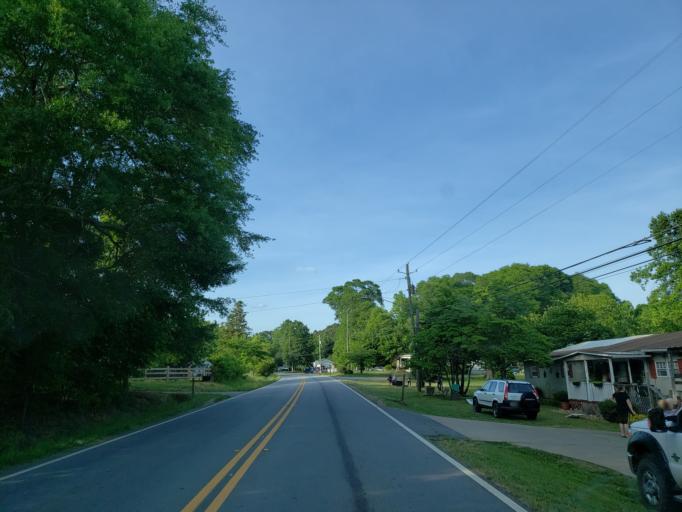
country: US
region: Georgia
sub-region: Carroll County
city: Bowdon
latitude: 33.5247
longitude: -85.2564
